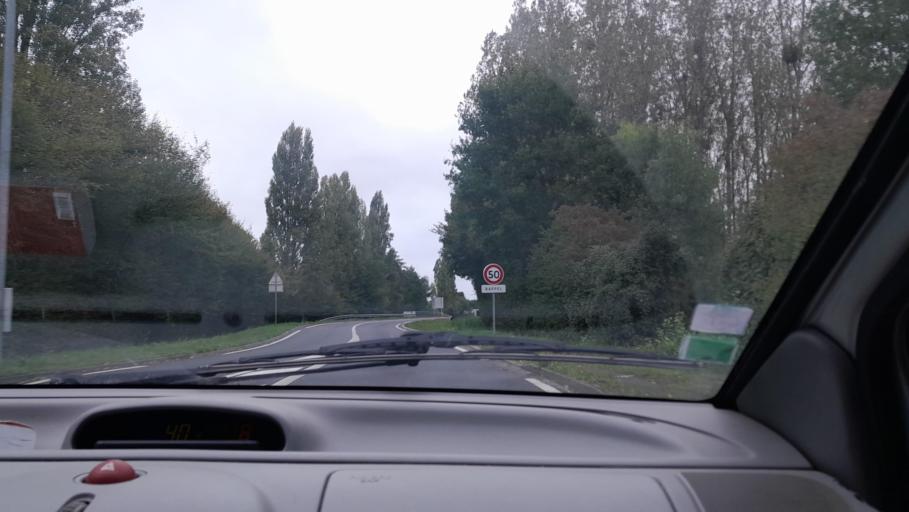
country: FR
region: Pays de la Loire
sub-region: Departement de la Loire-Atlantique
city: Saint-Mars-la-Jaille
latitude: 47.5254
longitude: -1.1760
